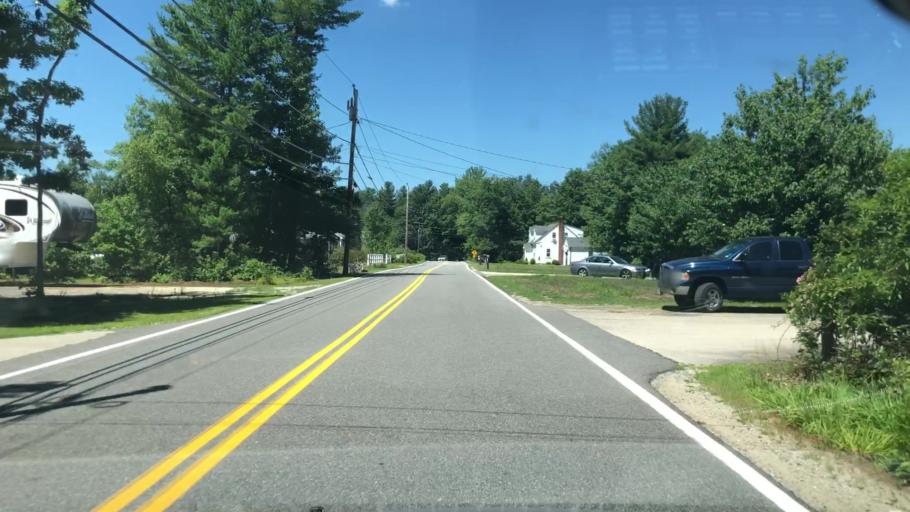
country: US
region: New Hampshire
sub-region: Hillsborough County
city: Milford
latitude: 42.8382
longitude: -71.6013
